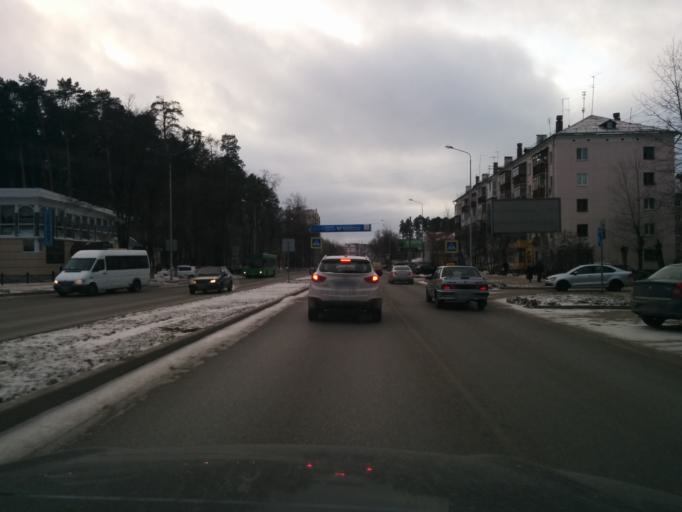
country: RU
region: Perm
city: Kultayevo
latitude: 58.0117
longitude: 55.9698
